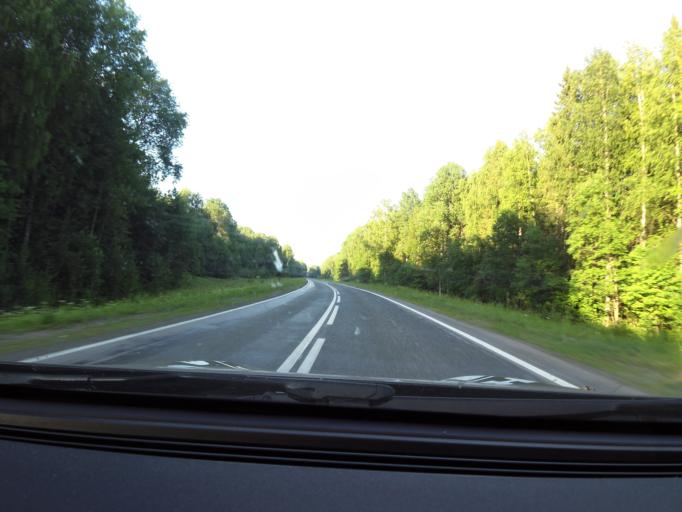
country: RU
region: Kirov
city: Kostino
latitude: 58.6400
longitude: 53.8126
